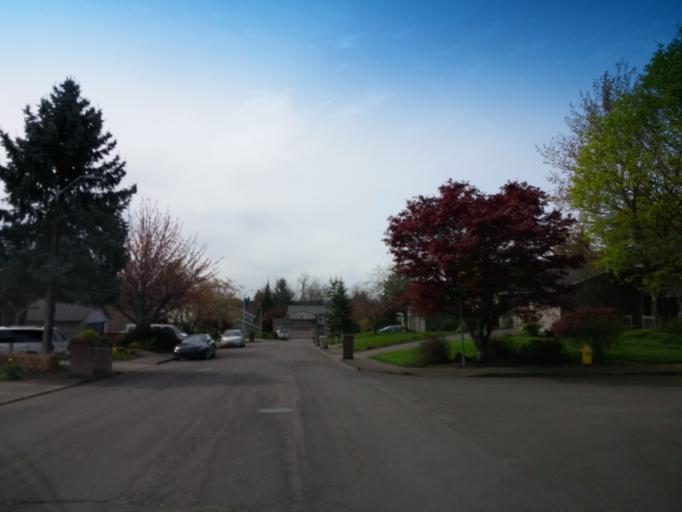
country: US
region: Oregon
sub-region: Washington County
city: Cedar Mill
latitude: 45.5288
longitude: -122.8024
